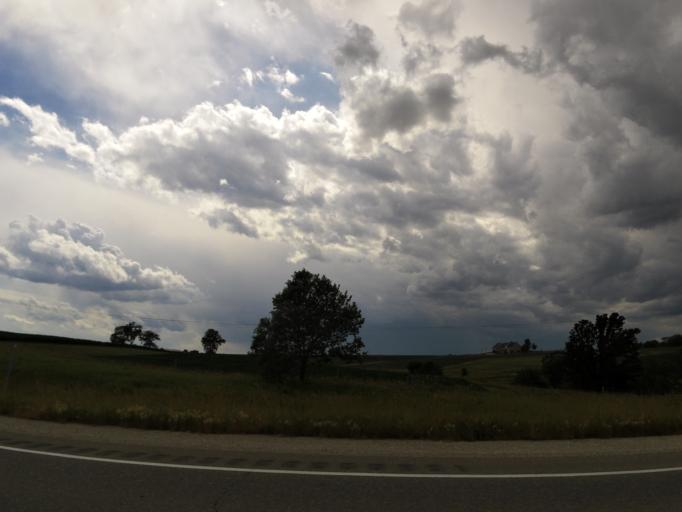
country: US
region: Iowa
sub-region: Washington County
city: Washington
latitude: 41.3756
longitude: -91.5512
